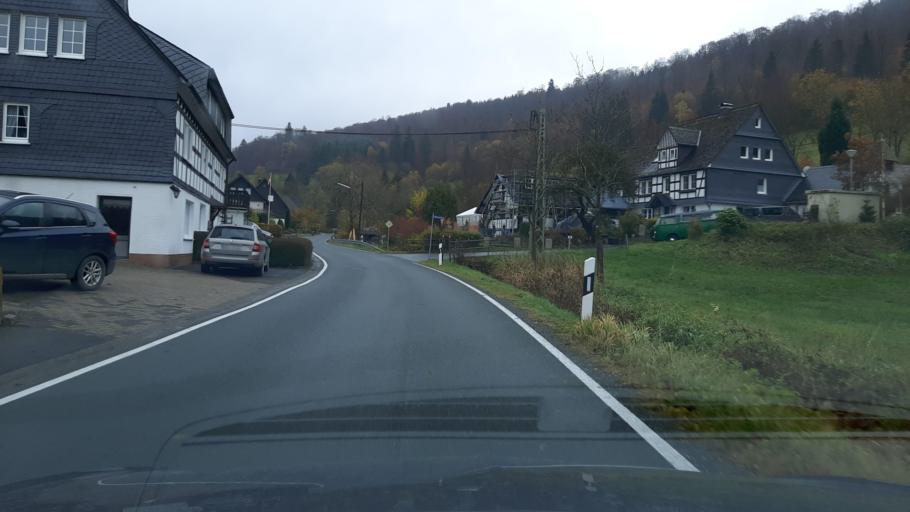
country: DE
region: North Rhine-Westphalia
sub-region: Regierungsbezirk Arnsberg
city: Bad Fredeburg
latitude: 51.1961
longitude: 8.4123
